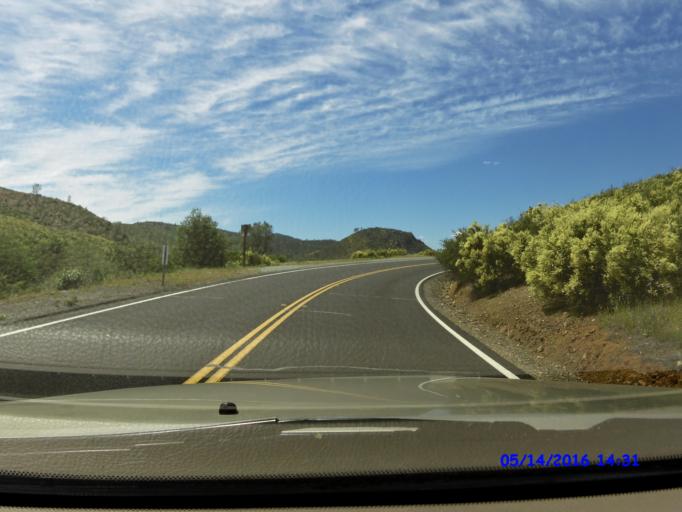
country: US
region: California
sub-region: Tuolumne County
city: Tuolumne City
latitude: 37.7599
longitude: -120.2529
